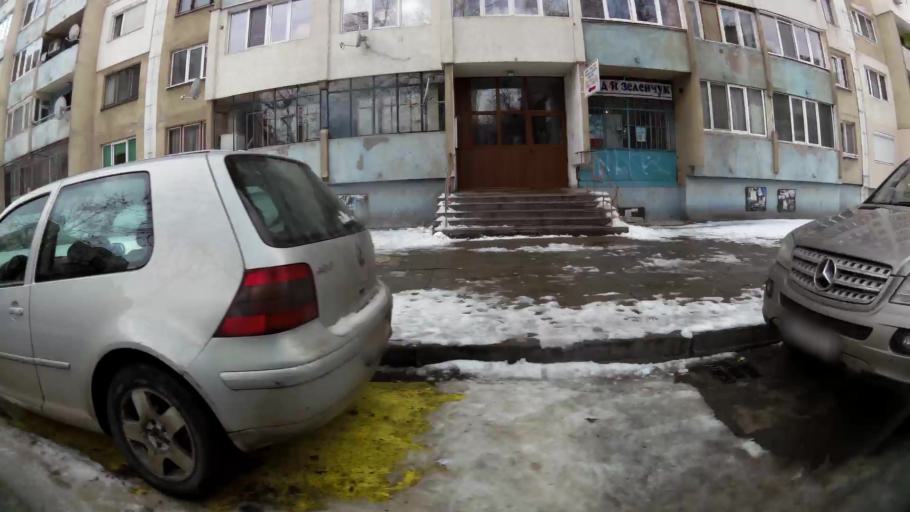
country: BG
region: Sofia-Capital
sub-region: Stolichna Obshtina
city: Sofia
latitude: 42.7008
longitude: 23.3563
